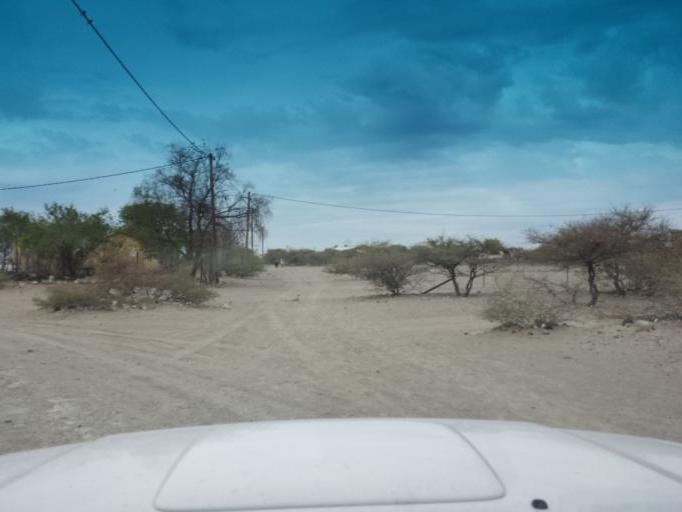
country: BW
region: Central
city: Mopipi
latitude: -21.2031
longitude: 24.8607
